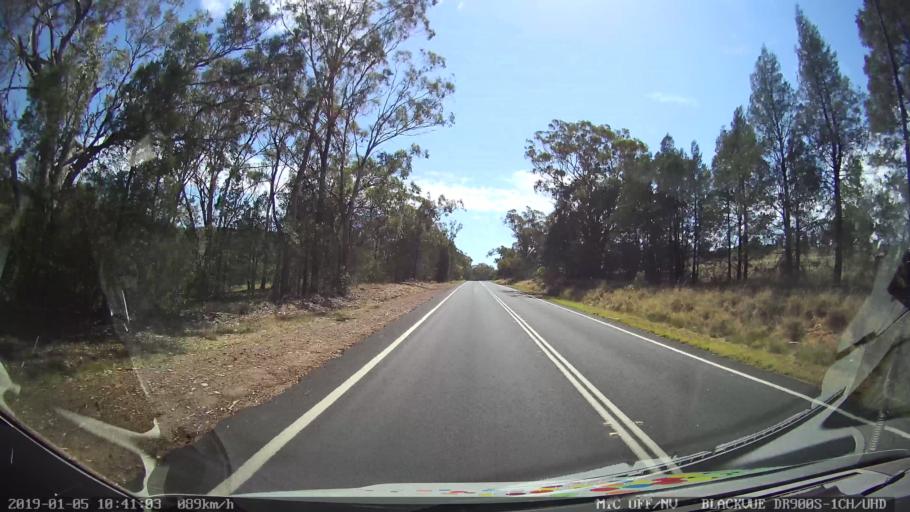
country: AU
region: New South Wales
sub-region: Warrumbungle Shire
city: Coonabarabran
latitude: -31.4658
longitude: 148.9536
